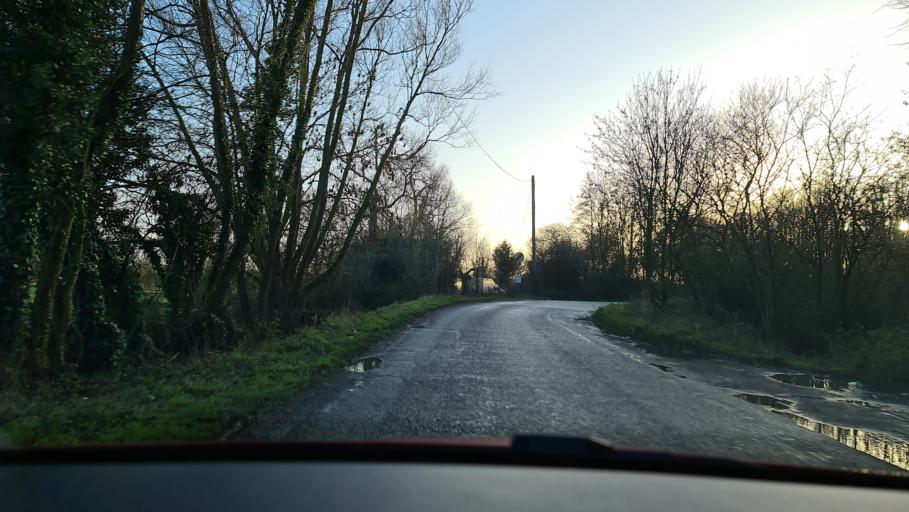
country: GB
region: England
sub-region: Northamptonshire
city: Deanshanger
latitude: 52.0515
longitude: -0.8724
